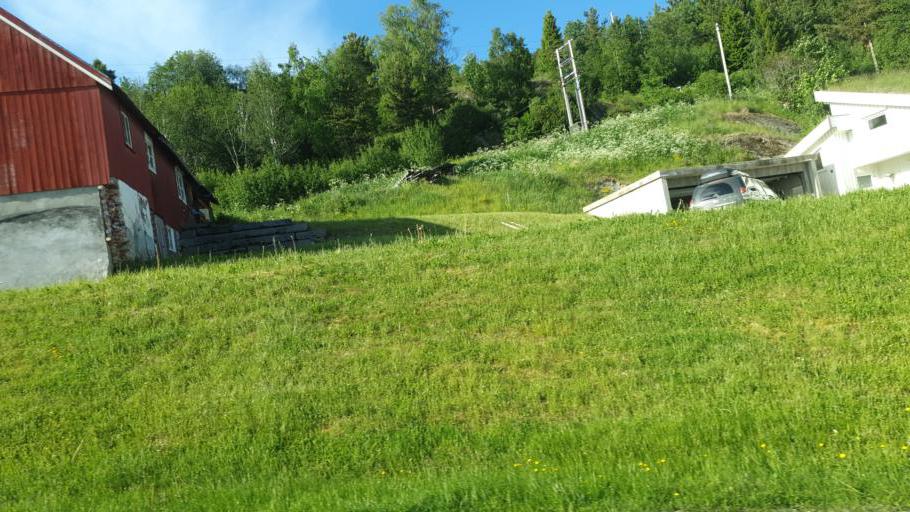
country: NO
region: Sor-Trondelag
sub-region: Rissa
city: Rissa
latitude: 63.4972
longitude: 10.0955
